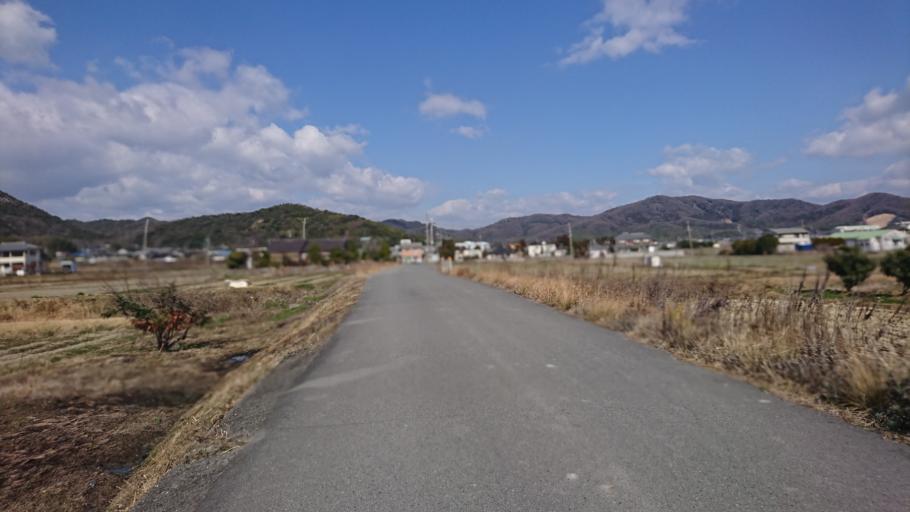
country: JP
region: Hyogo
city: Kakogawacho-honmachi
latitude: 34.8100
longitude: 134.8055
